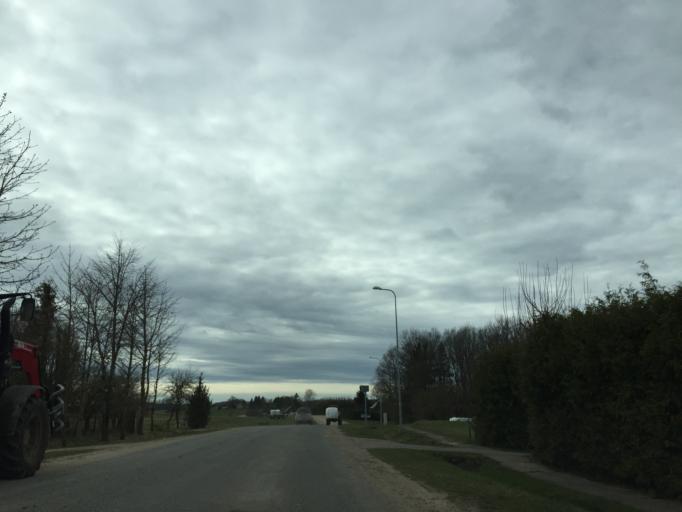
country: LT
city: Silale
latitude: 55.6198
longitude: 22.2178
